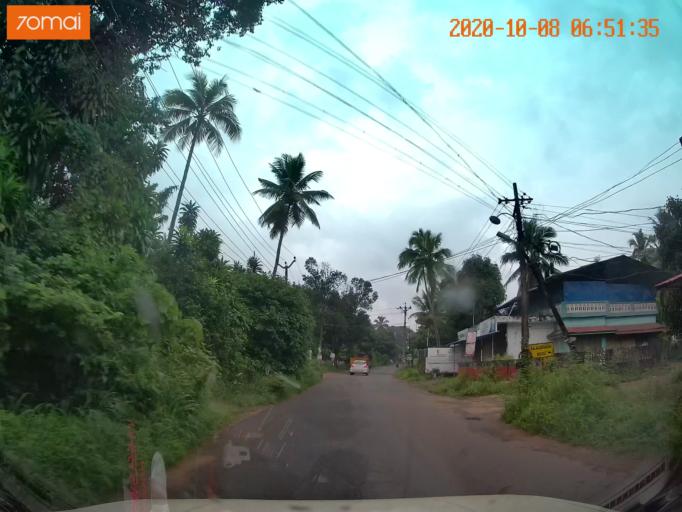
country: IN
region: Kerala
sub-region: Thrissur District
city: Kunnamkulam
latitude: 10.6898
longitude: 76.0926
